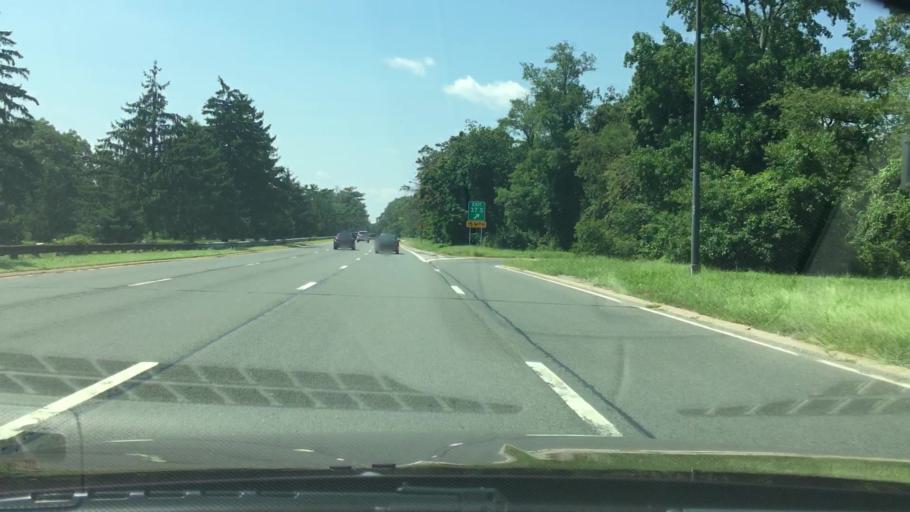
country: US
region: New York
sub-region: Suffolk County
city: West Babylon
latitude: 40.7324
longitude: -73.3465
